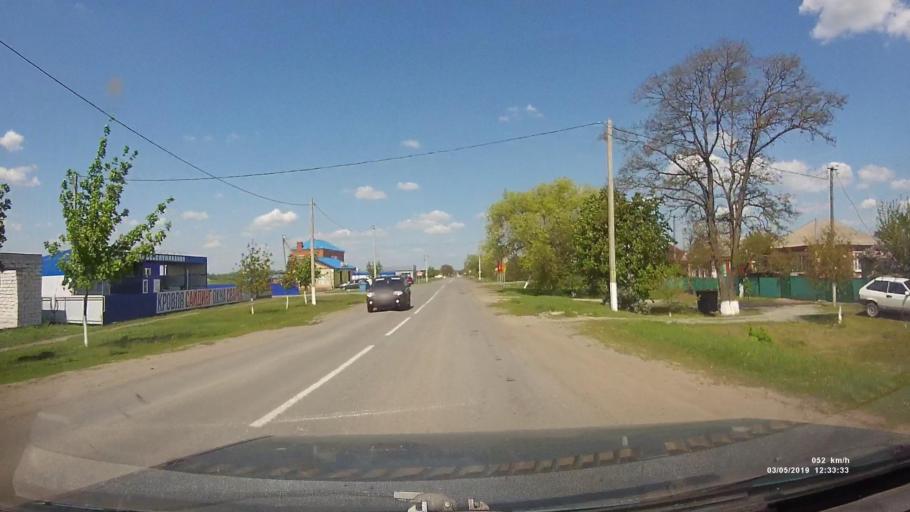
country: RU
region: Rostov
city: Semikarakorsk
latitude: 47.5138
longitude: 40.7716
